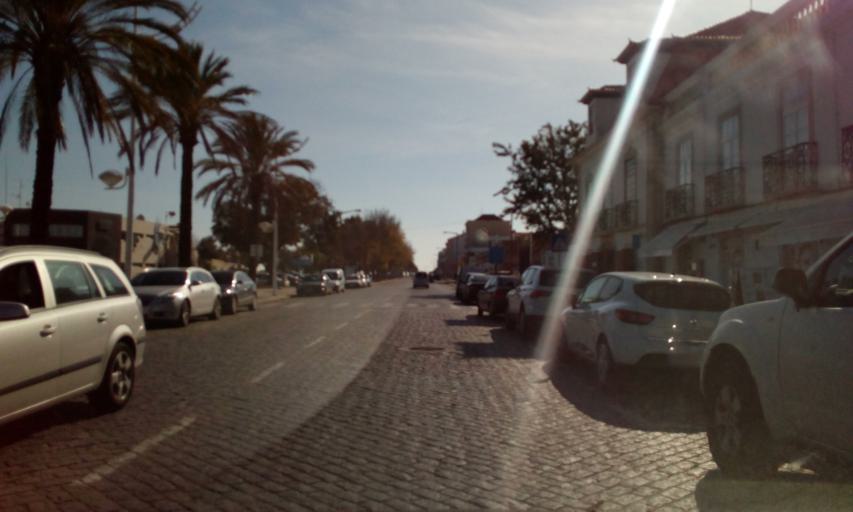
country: PT
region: Faro
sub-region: Vila Real de Santo Antonio
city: Vila Real de Santo Antonio
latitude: 37.1935
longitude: -7.4140
